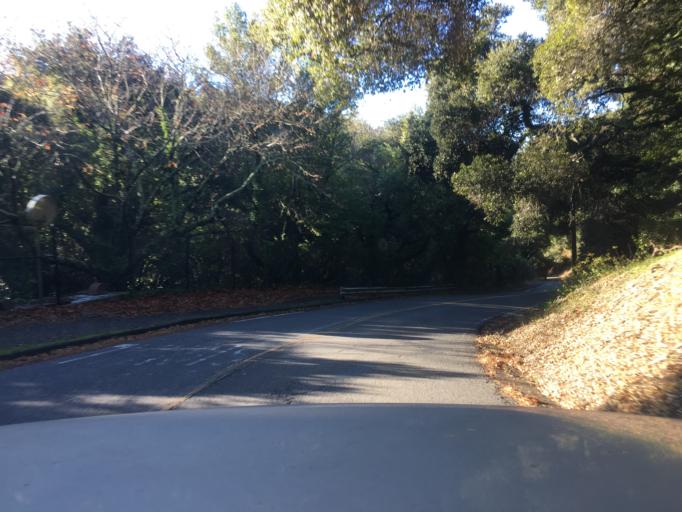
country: US
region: California
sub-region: Alameda County
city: Berkeley
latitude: 37.8747
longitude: -122.2391
